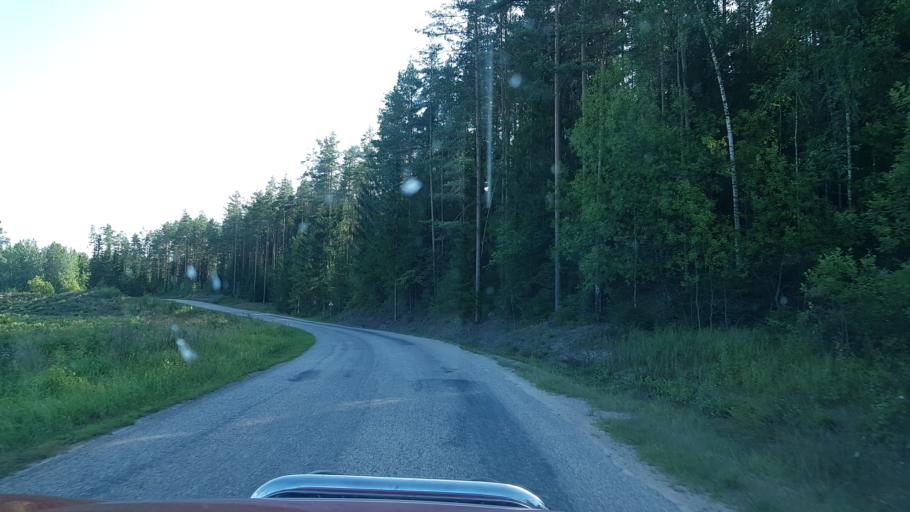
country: EE
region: Vorumaa
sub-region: Voru linn
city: Voru
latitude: 57.8897
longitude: 27.1060
